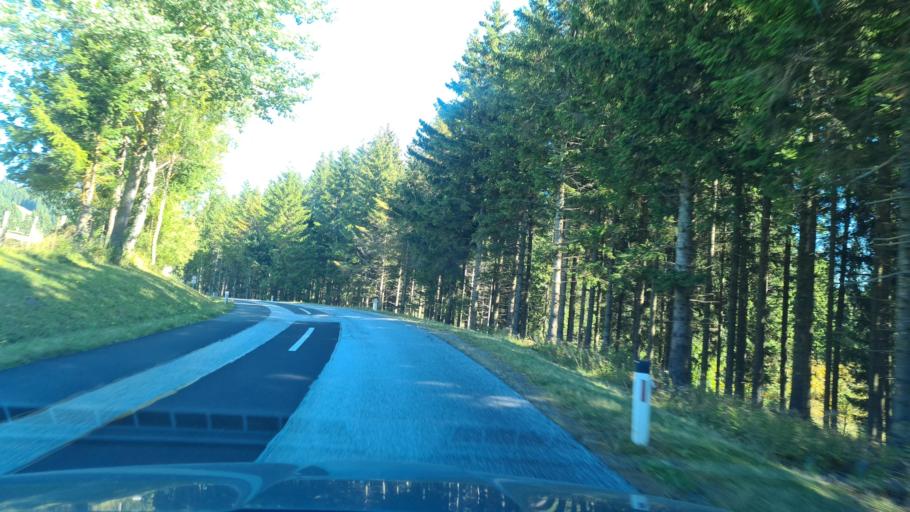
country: AT
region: Styria
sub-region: Politischer Bezirk Weiz
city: Gasen
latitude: 47.3511
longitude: 15.5127
